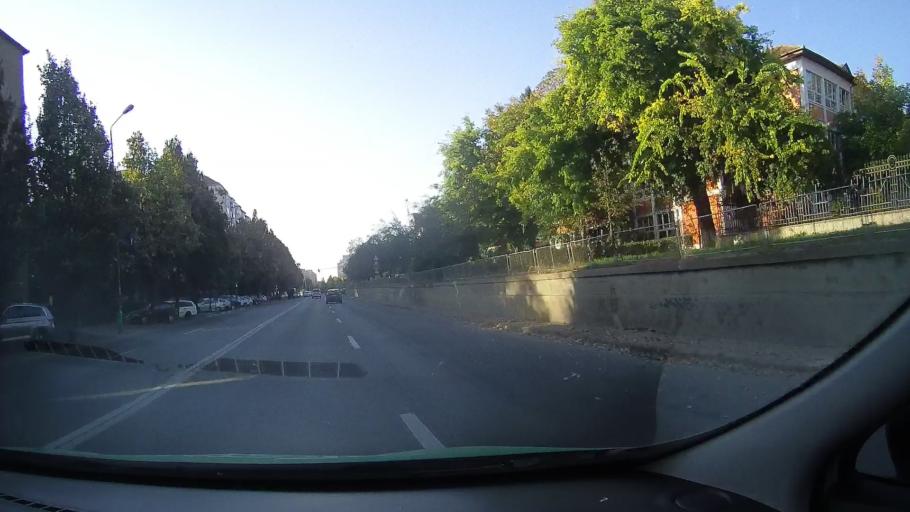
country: RO
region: Bihor
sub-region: Comuna Biharea
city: Oradea
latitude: 47.0679
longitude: 21.9286
